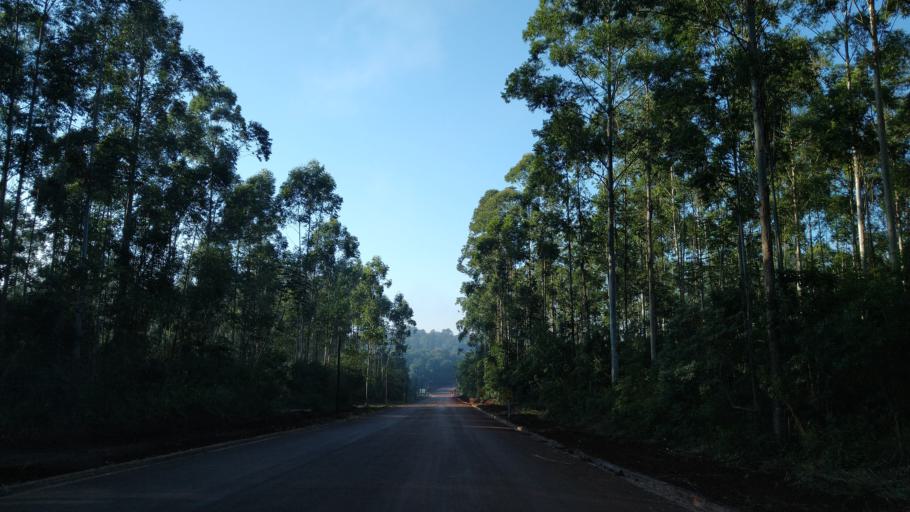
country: AR
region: Misiones
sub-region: Departamento de Montecarlo
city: Montecarlo
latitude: -26.5579
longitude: -54.7713
